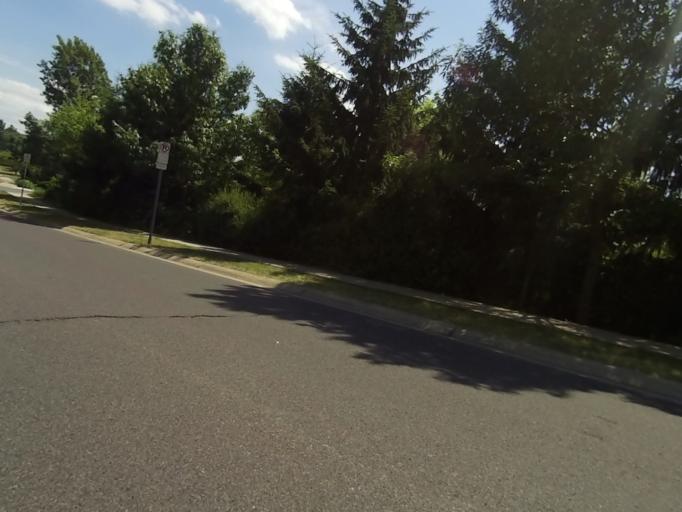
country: US
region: Pennsylvania
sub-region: Centre County
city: Park Forest Village
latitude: 40.7915
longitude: -77.9048
